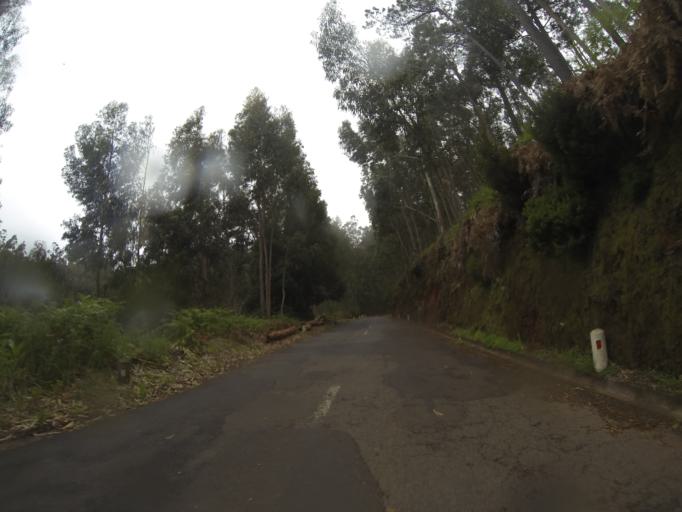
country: PT
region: Madeira
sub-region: Calheta
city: Estreito da Calheta
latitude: 32.7718
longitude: -17.1906
